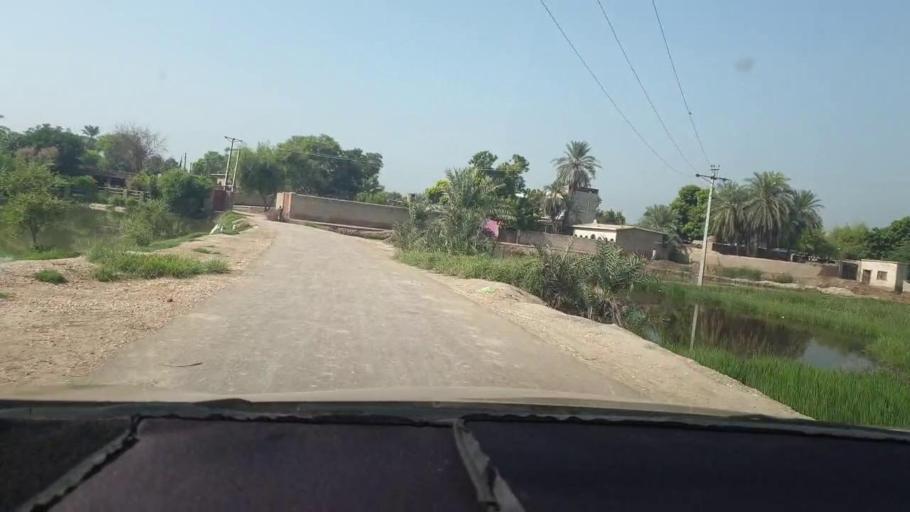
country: PK
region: Sindh
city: Kambar
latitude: 27.5733
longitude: 68.0745
